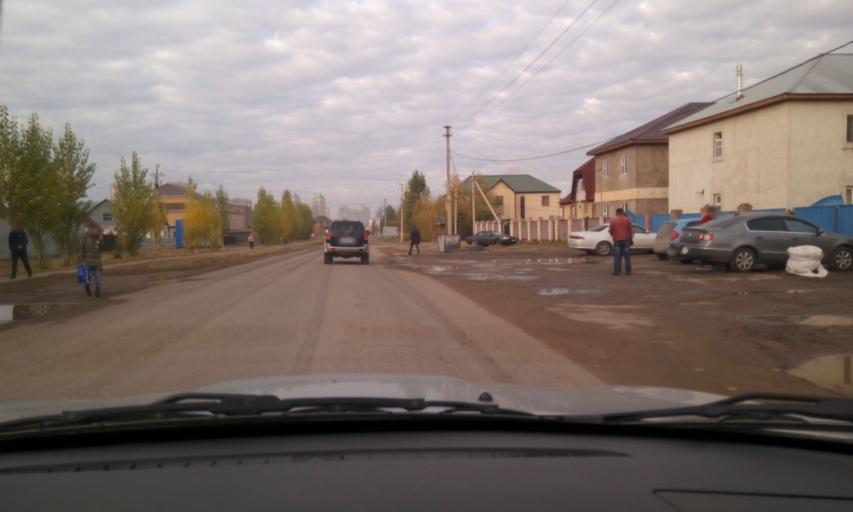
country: KZ
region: Astana Qalasy
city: Astana
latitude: 51.1370
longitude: 71.4896
